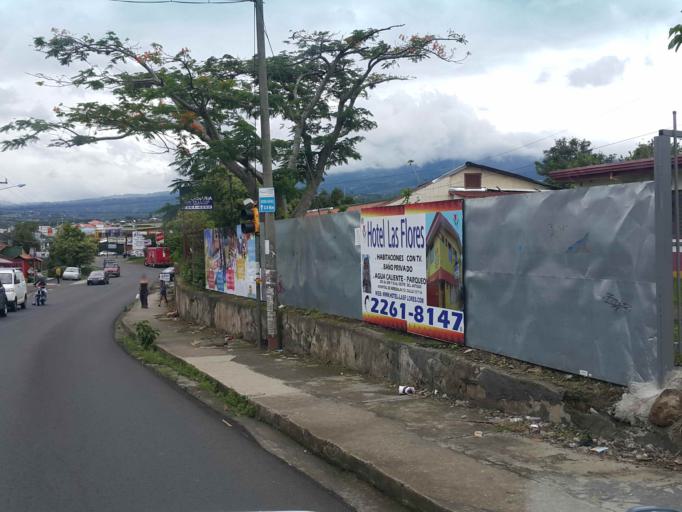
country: CR
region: Heredia
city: Heredia
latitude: 10.0108
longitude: -84.1192
